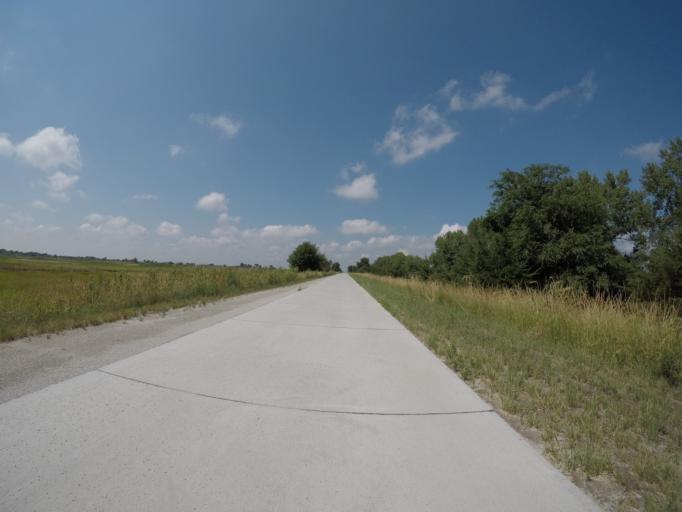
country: US
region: Nebraska
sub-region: Buffalo County
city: Kearney
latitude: 40.6688
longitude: -98.9897
